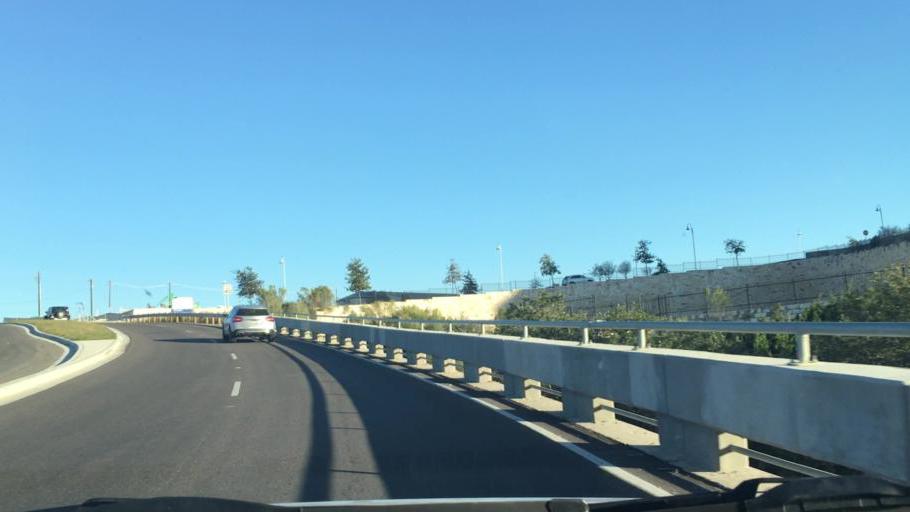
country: US
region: Texas
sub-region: Travis County
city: The Hills
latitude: 30.3344
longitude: -97.9716
